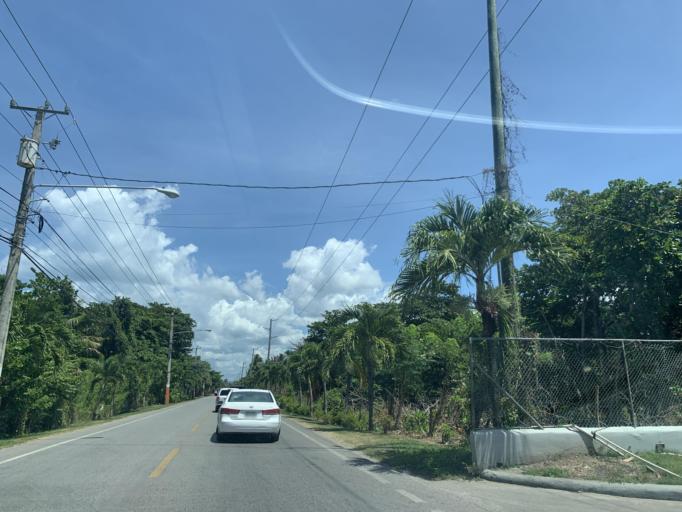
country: DO
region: Puerto Plata
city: Cabarete
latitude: 19.7425
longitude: -70.3933
